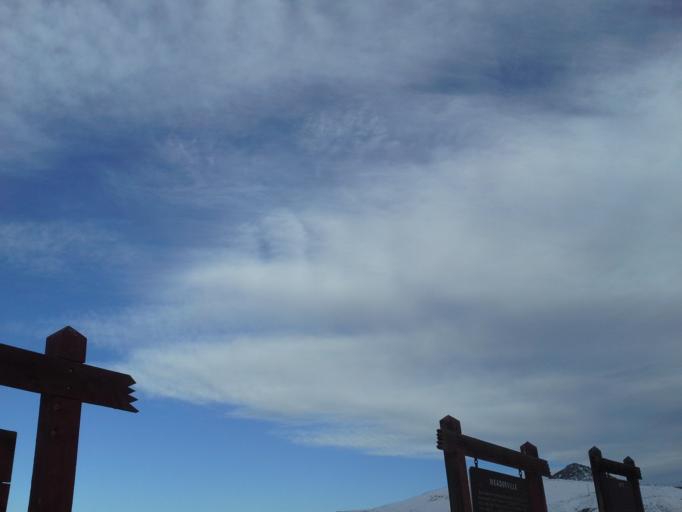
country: US
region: Montana
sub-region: Silver Bow County
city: Butte
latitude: 45.9910
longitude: -112.4752
